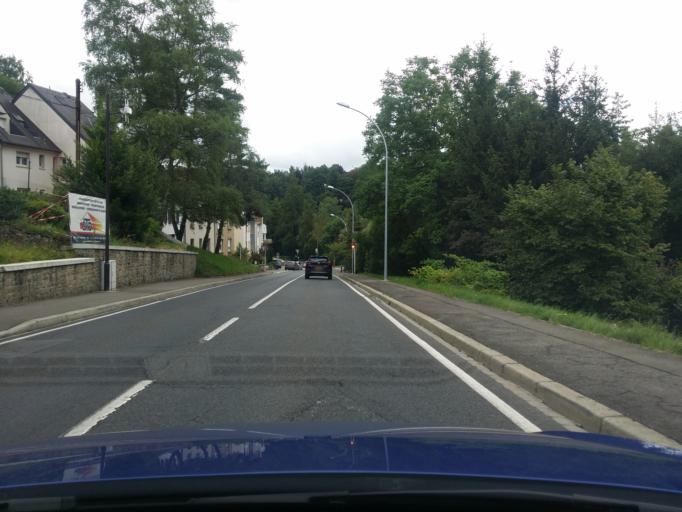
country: LU
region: Luxembourg
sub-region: Canton de Luxembourg
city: Luxembourg
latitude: 49.6027
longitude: 6.1449
